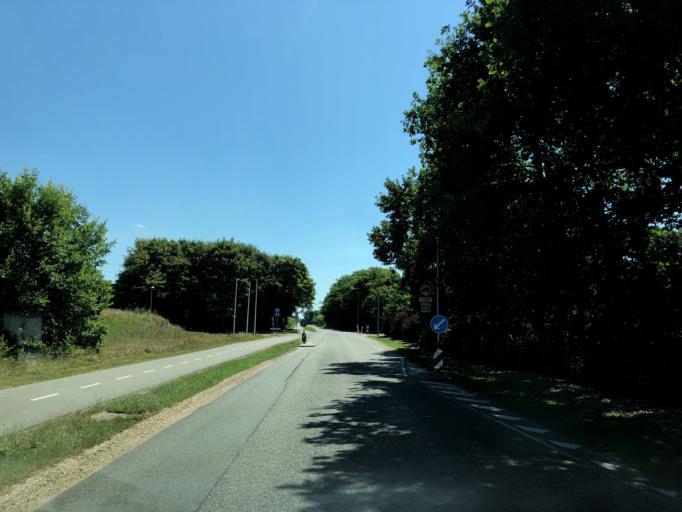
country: DK
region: Central Jutland
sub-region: Holstebro Kommune
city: Holstebro
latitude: 56.3432
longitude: 8.6704
